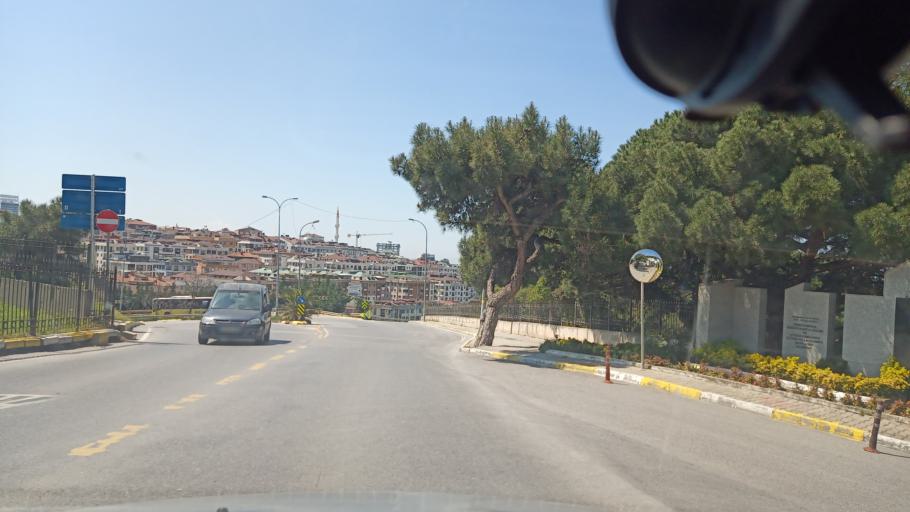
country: TR
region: Istanbul
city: Maltepe
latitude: 40.9465
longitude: 29.1442
